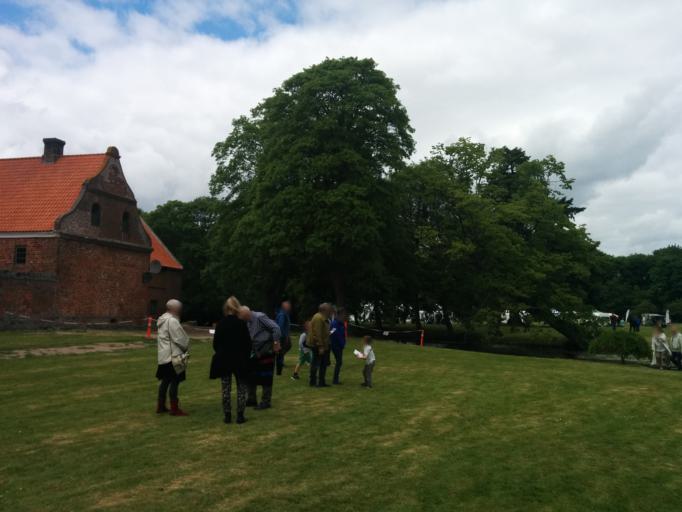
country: DK
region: Central Jutland
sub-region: Norddjurs Kommune
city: Auning
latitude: 56.3687
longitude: 10.4101
